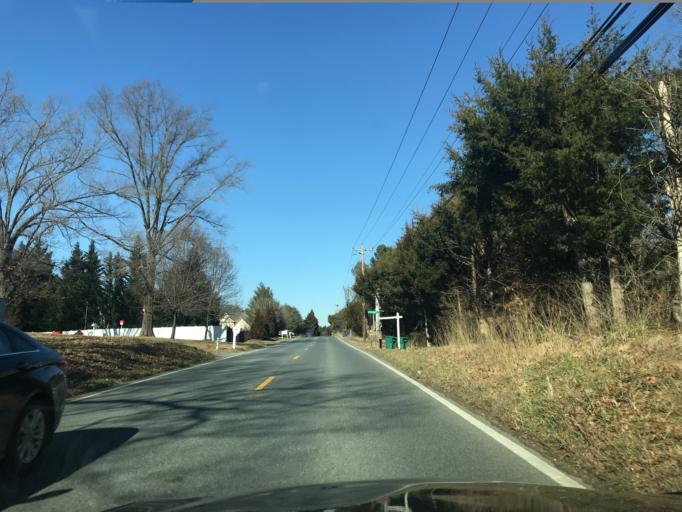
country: US
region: Maryland
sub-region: Charles County
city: Bennsville
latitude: 38.6296
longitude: -77.0150
